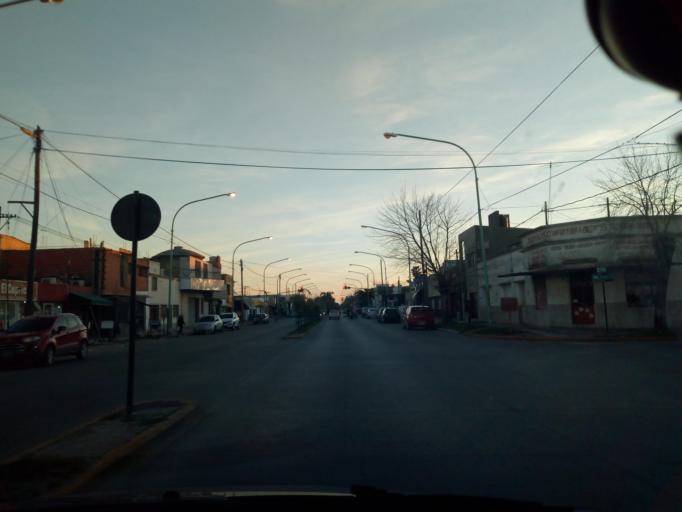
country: AR
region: Buenos Aires
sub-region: Partido de Ensenada
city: Ensenada
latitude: -34.8668
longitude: -57.9071
